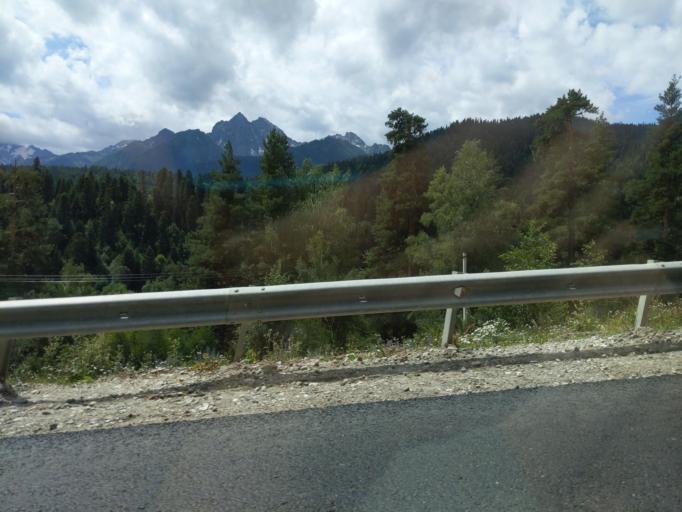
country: RU
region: Karachayevo-Cherkesiya
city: Nizhniy Arkhyz
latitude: 43.5370
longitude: 41.2169
